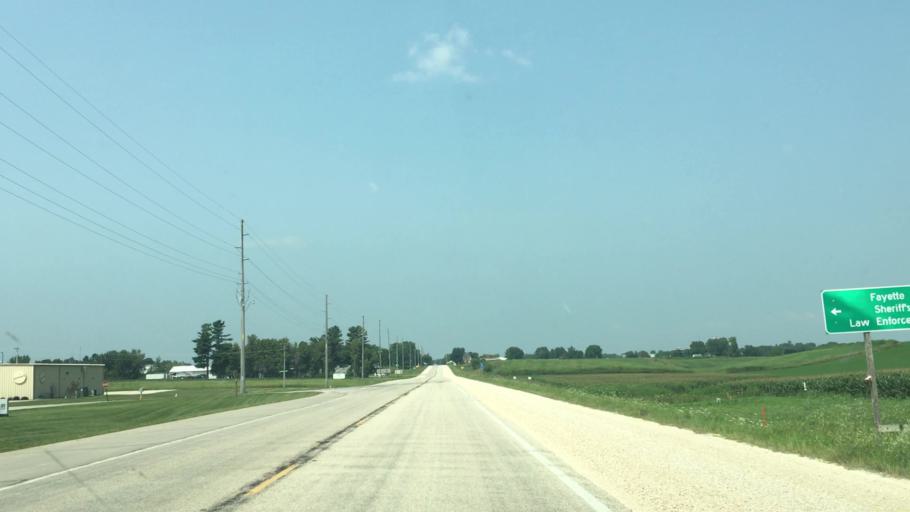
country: US
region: Iowa
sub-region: Fayette County
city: West Union
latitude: 42.9426
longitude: -91.8142
